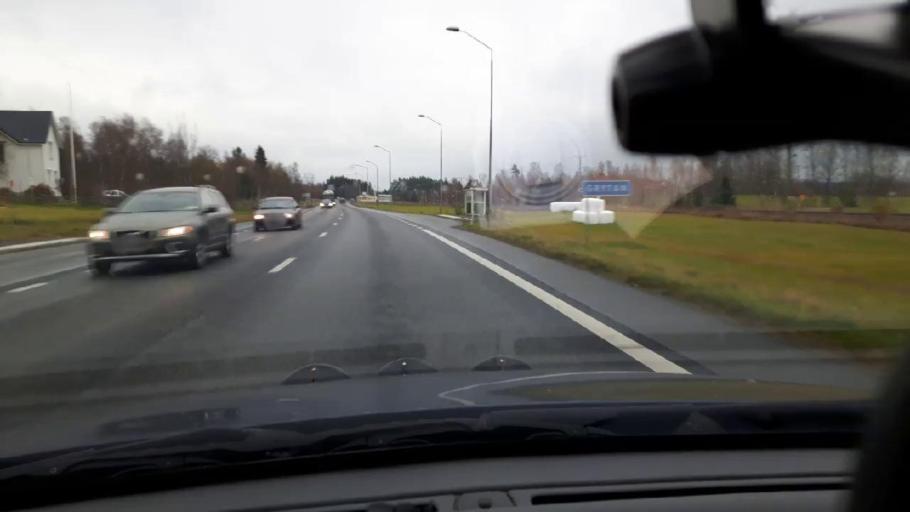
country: SE
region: Jaemtland
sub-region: OEstersunds Kommun
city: Brunflo
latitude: 63.0984
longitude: 14.7977
